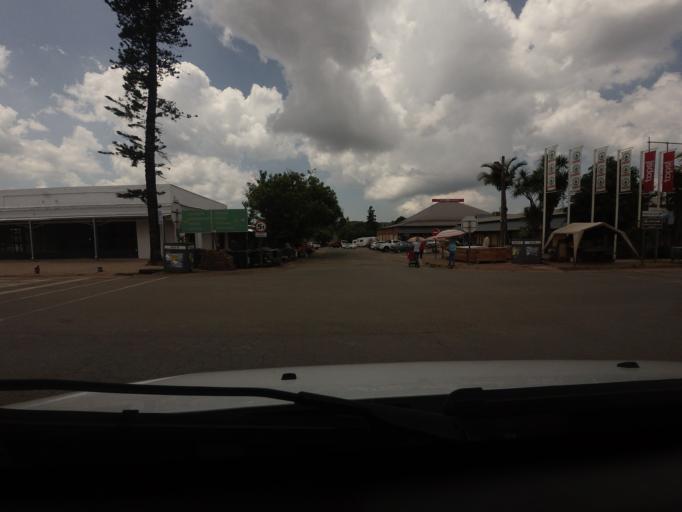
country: ZA
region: Mpumalanga
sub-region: Ehlanzeni District
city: Graksop
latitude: -24.9337
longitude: 30.8406
